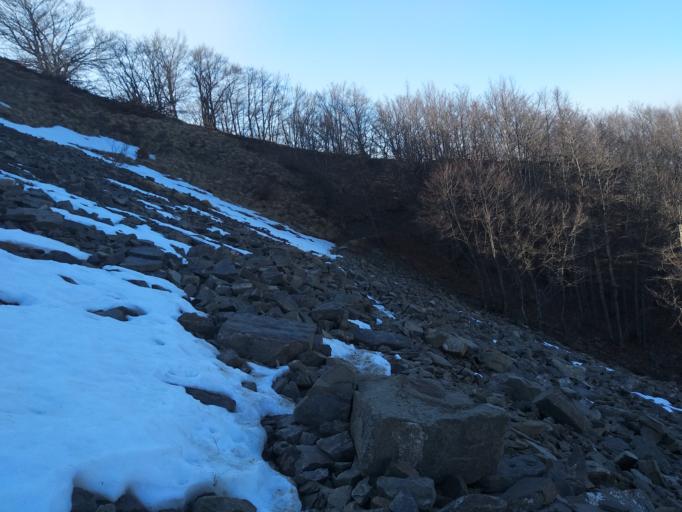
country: IT
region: Emilia-Romagna
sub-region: Provincia di Reggio Emilia
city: Busana
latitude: 44.3816
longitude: 10.2948
